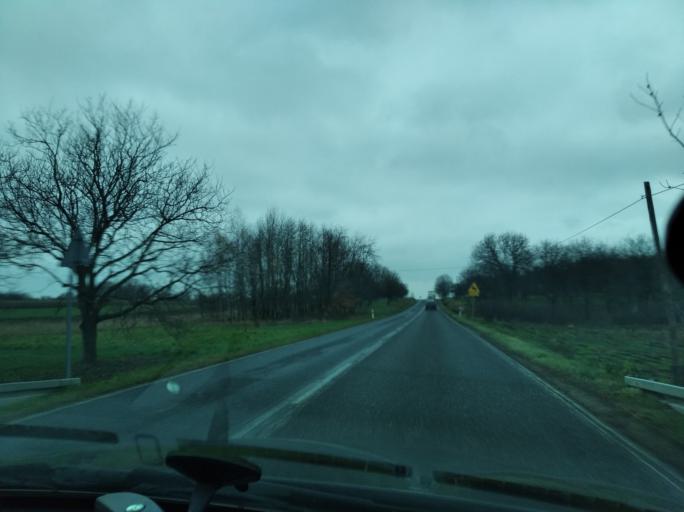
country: PL
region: Subcarpathian Voivodeship
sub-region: Powiat przeworski
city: Sietesz
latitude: 49.9979
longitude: 22.3646
